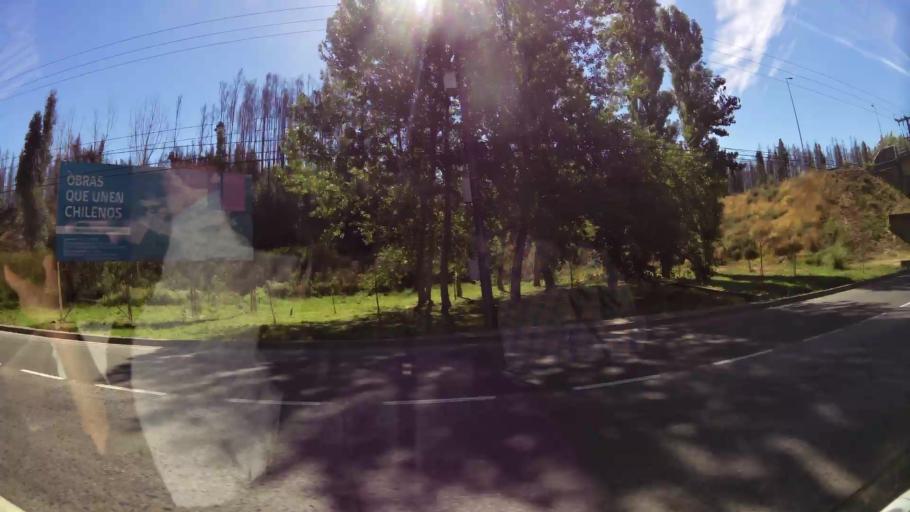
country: CL
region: Biobio
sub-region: Provincia de Concepcion
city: Penco
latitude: -36.7552
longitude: -73.0015
